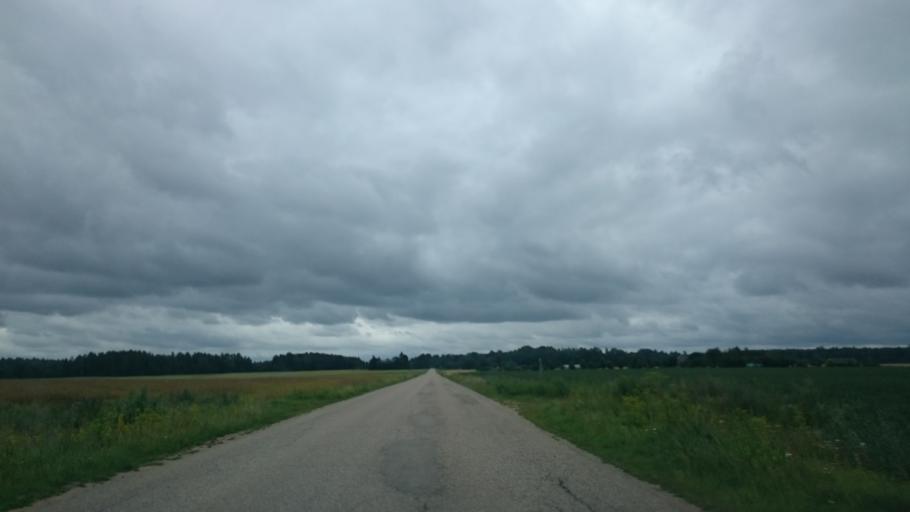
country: LV
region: Aizpute
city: Aizpute
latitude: 56.7161
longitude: 21.4596
